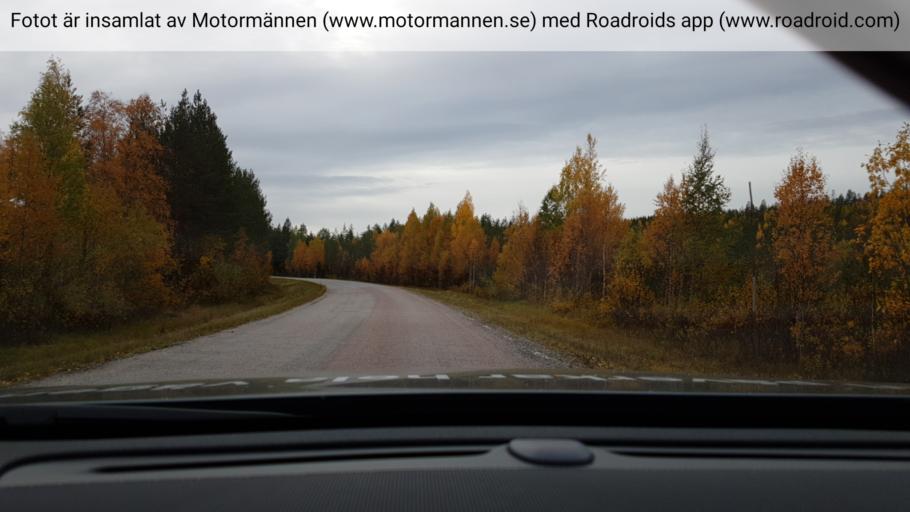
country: SE
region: Norrbotten
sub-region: Overkalix Kommun
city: OEverkalix
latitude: 66.2454
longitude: 23.0034
